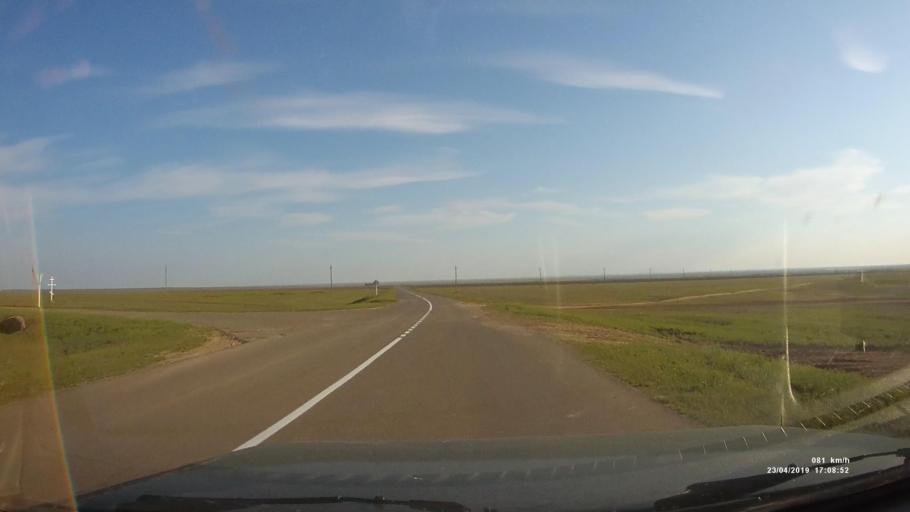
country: RU
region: Kalmykiya
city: Priyutnoye
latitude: 46.2662
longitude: 43.4845
